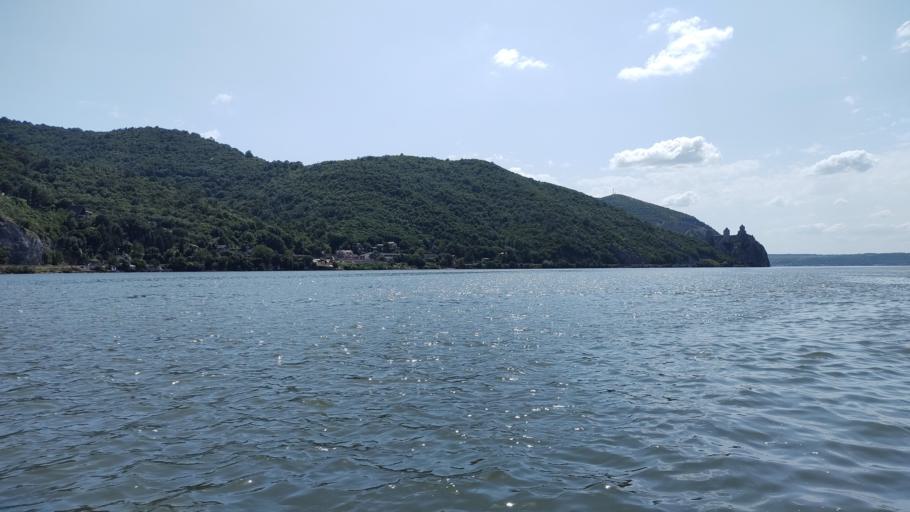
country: RO
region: Caras-Severin
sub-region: Comuna Pescari
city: Coronini
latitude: 44.6641
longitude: 21.6941
